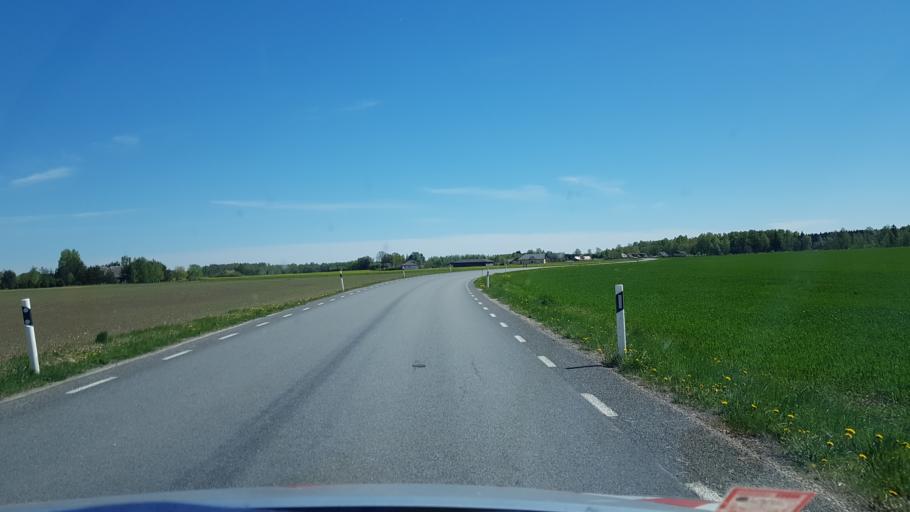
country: EE
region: Tartu
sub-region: UElenurme vald
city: Ulenurme
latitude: 58.3165
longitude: 26.6391
